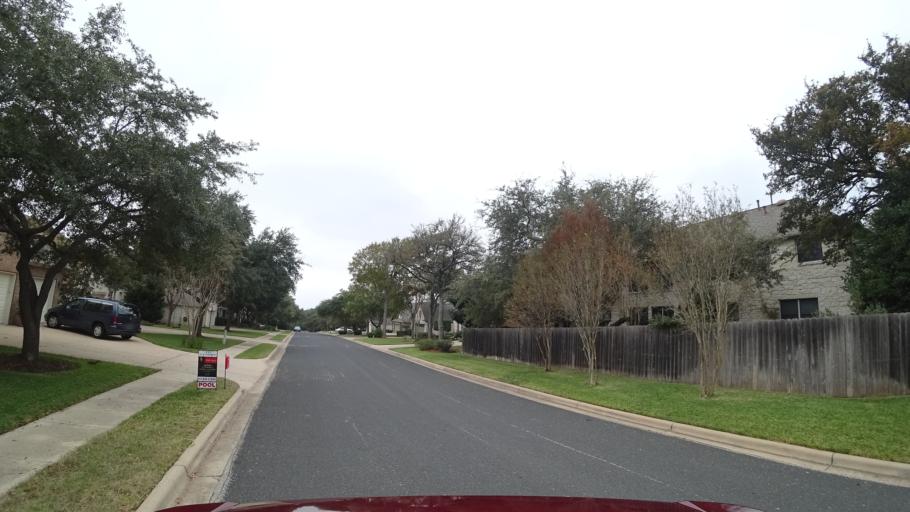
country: US
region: Texas
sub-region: Williamson County
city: Anderson Mill
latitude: 30.4493
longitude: -97.8180
